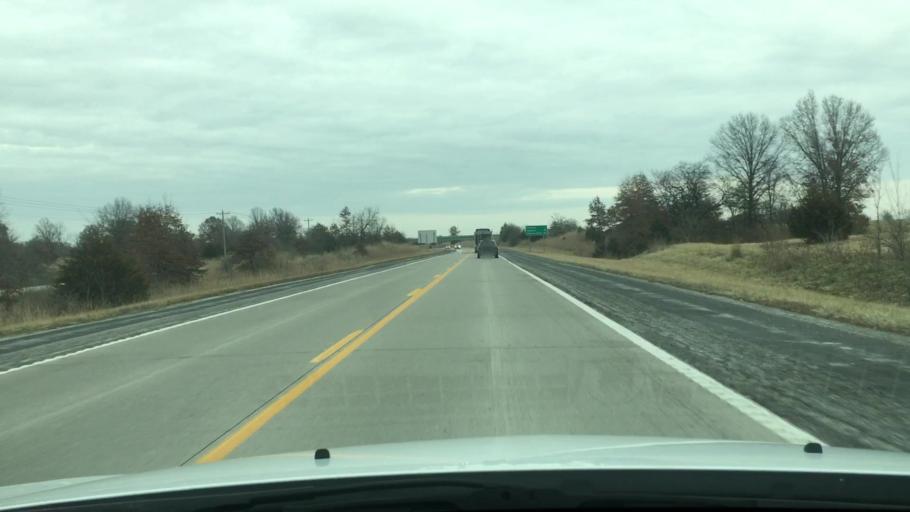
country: US
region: Missouri
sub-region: Audrain County
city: Mexico
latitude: 39.1240
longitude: -91.8738
